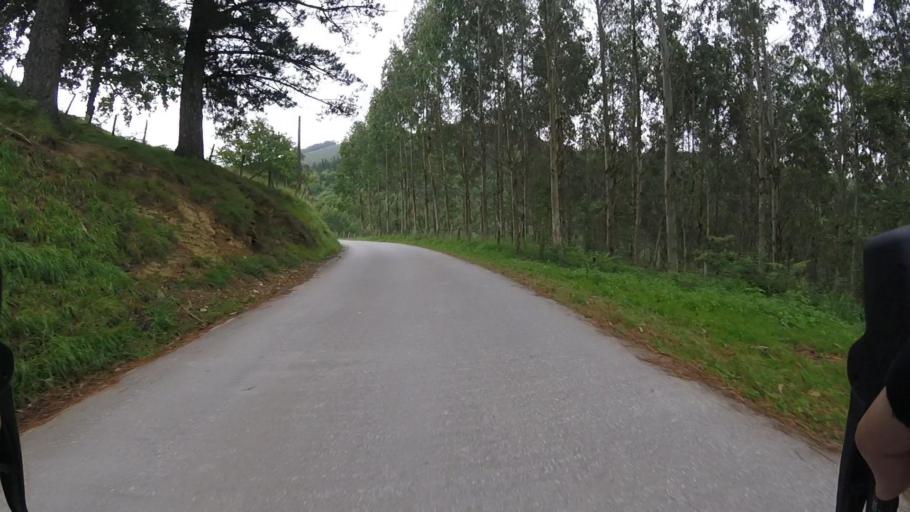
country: ES
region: Basque Country
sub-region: Provincia de Guipuzcoa
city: Errenteria
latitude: 43.2588
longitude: -1.8911
